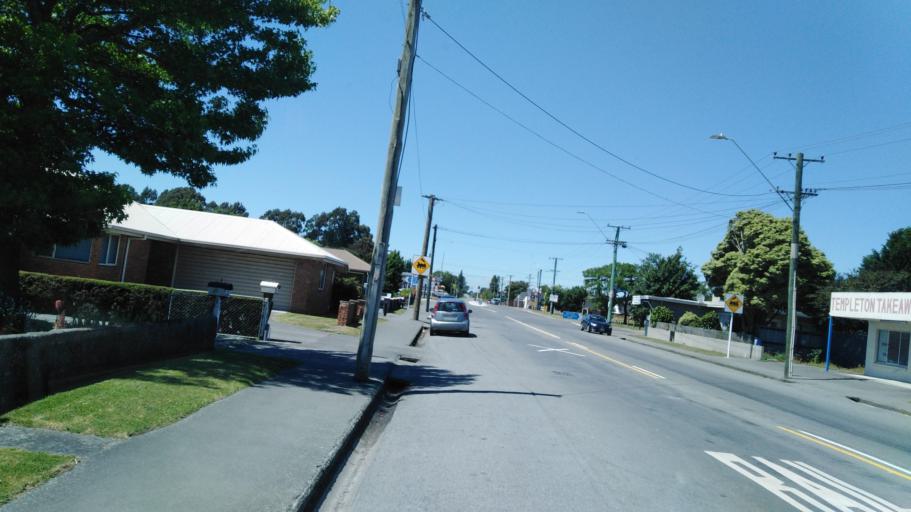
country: NZ
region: Canterbury
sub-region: Selwyn District
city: Prebbleton
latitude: -43.5533
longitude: 172.4735
